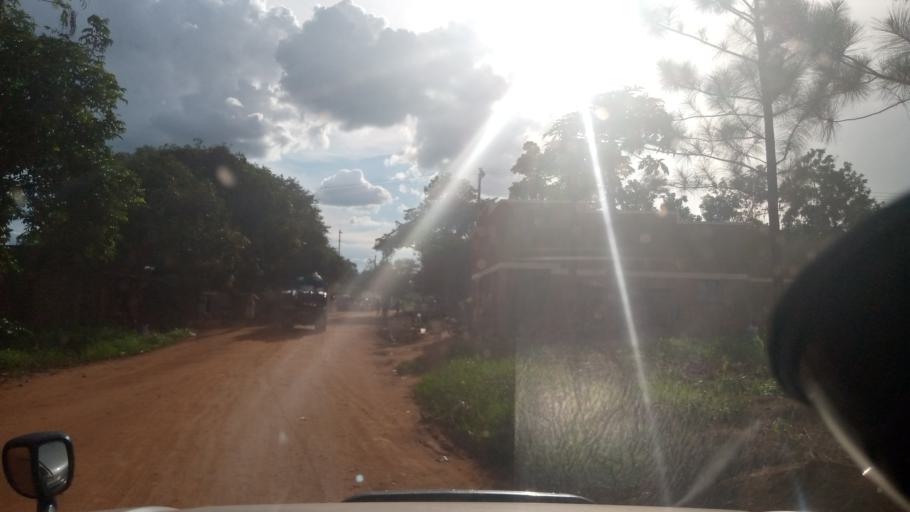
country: UG
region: Northern Region
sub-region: Lira District
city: Lira
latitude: 2.2275
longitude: 32.8965
